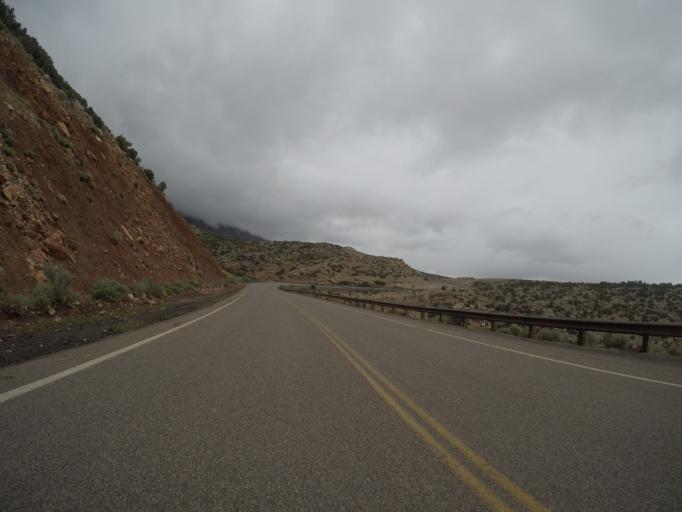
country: US
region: Wyoming
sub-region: Big Horn County
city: Lovell
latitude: 45.0450
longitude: -108.2528
